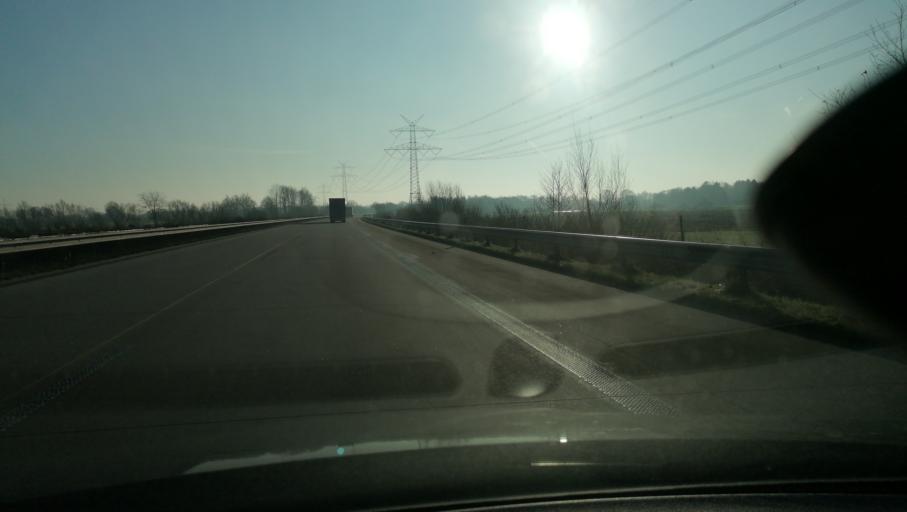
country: DE
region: Schleswig-Holstein
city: Klein Offenseth-Sparrieshoop
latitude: 53.7902
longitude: 9.6989
